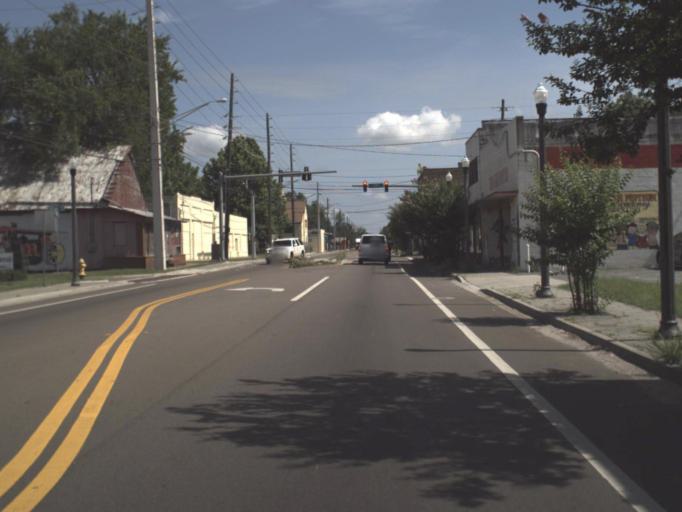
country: US
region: Florida
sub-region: Duval County
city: Jacksonville
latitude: 30.3223
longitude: -81.7054
